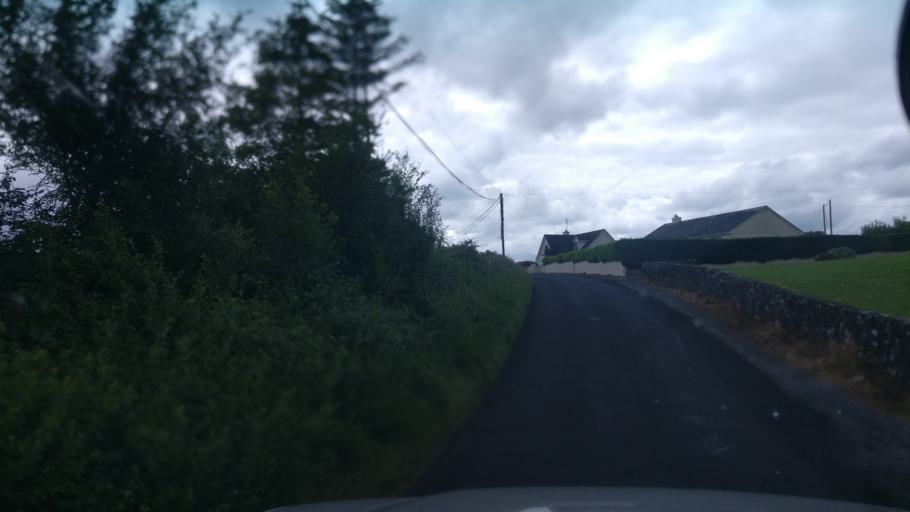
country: IE
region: Connaught
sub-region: County Galway
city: Loughrea
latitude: 53.1720
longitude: -8.5693
